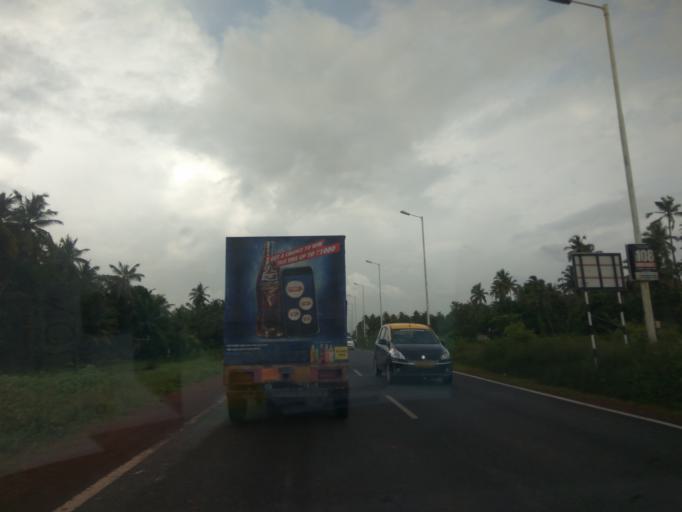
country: IN
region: Goa
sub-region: North Goa
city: Goa Velha
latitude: 15.4382
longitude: 73.8806
